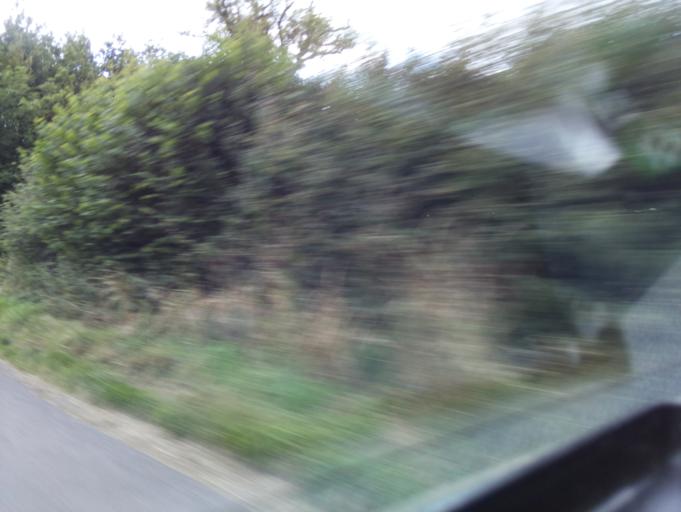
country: GB
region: England
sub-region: Gloucestershire
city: Chalford
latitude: 51.7717
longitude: -2.0914
